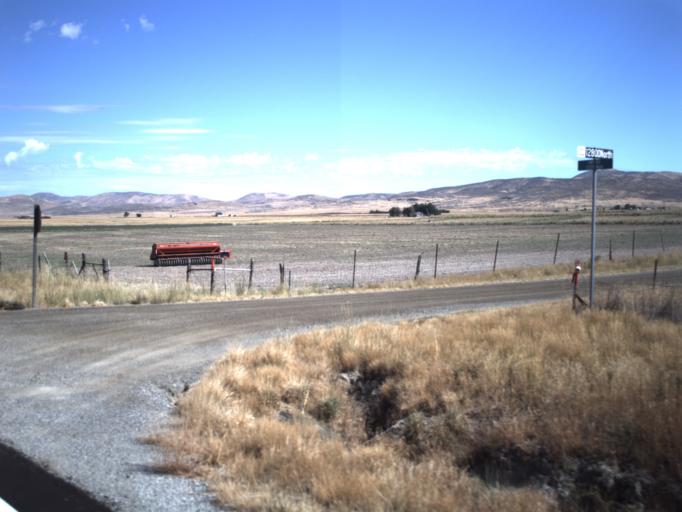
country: US
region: Utah
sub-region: Box Elder County
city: Tremonton
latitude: 41.7368
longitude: -112.4341
